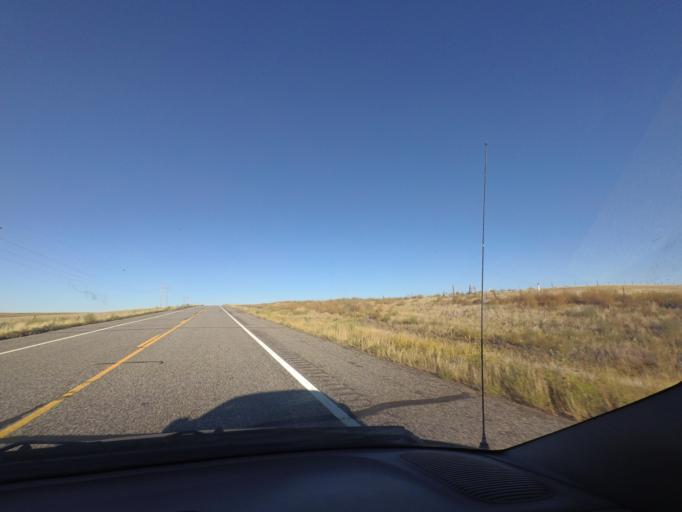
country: US
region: Colorado
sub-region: Lincoln County
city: Limon
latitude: 39.7399
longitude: -103.5550
